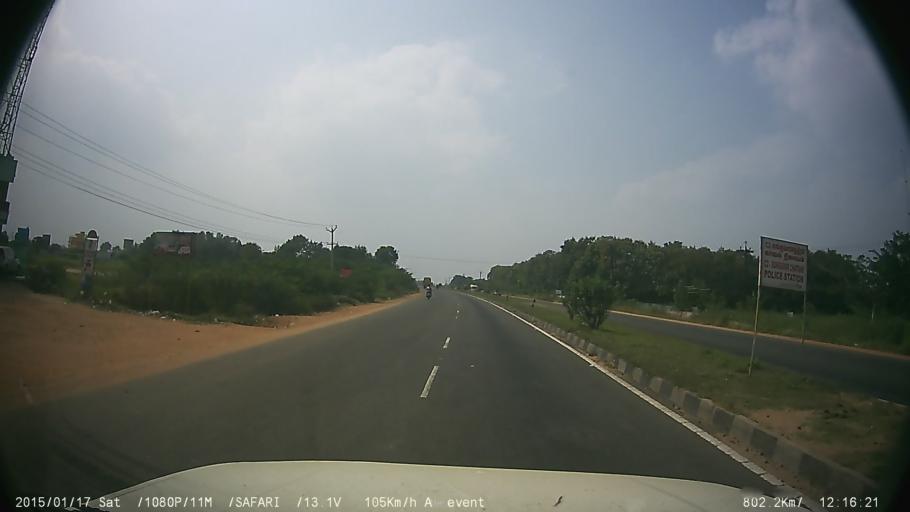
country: IN
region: Tamil Nadu
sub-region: Kancheepuram
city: Sriperumbudur
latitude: 12.9167
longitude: 79.8608
